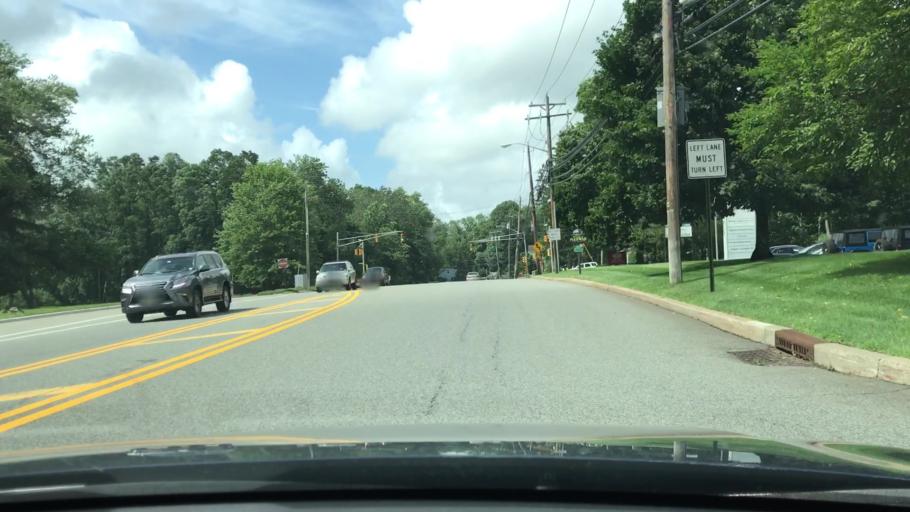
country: US
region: New Jersey
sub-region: Bergen County
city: Wyckoff
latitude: 41.0244
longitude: -74.1677
